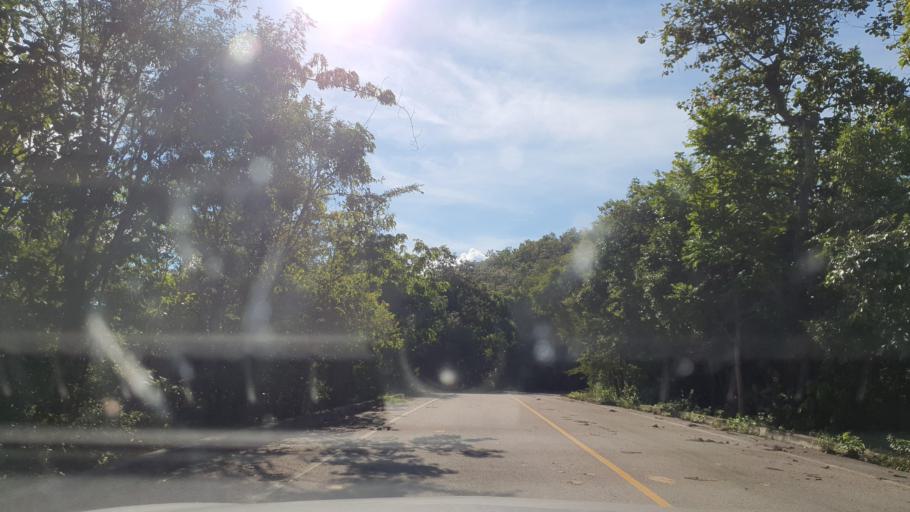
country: TH
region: Chiang Mai
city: Mae On
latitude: 18.7687
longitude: 99.2899
